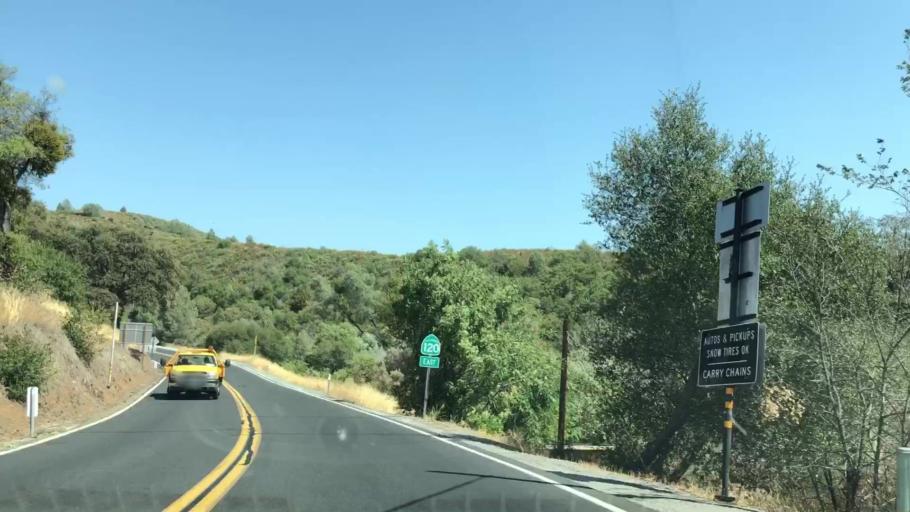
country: US
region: California
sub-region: Tuolumne County
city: Tuolumne City
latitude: 37.8139
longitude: -120.2718
